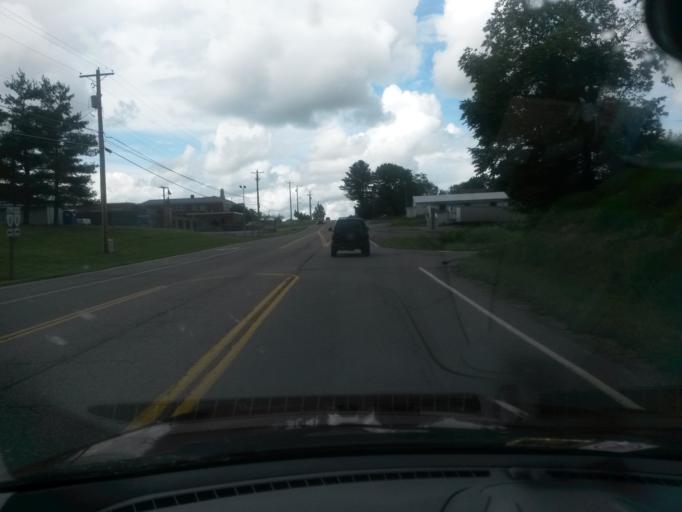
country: US
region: Virginia
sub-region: Montgomery County
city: Christiansburg
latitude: 37.0592
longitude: -80.4413
